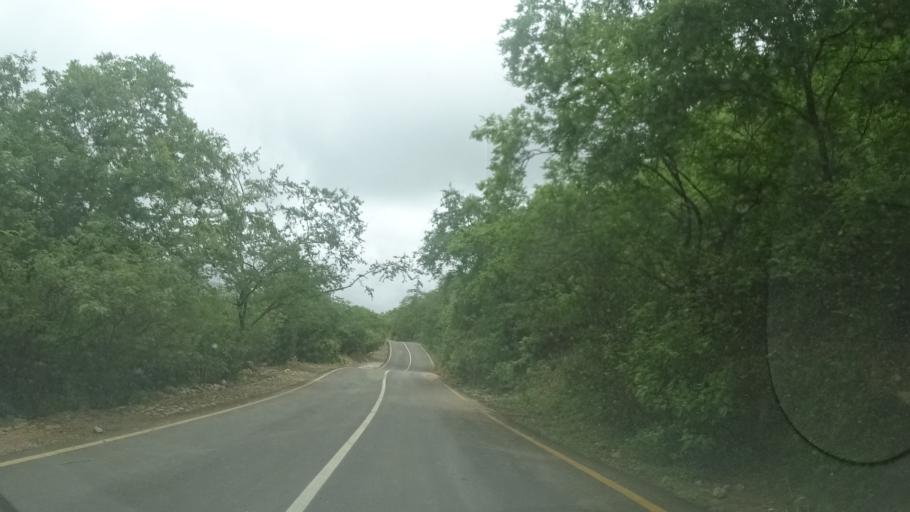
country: OM
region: Zufar
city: Salalah
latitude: 17.1018
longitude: 54.3455
